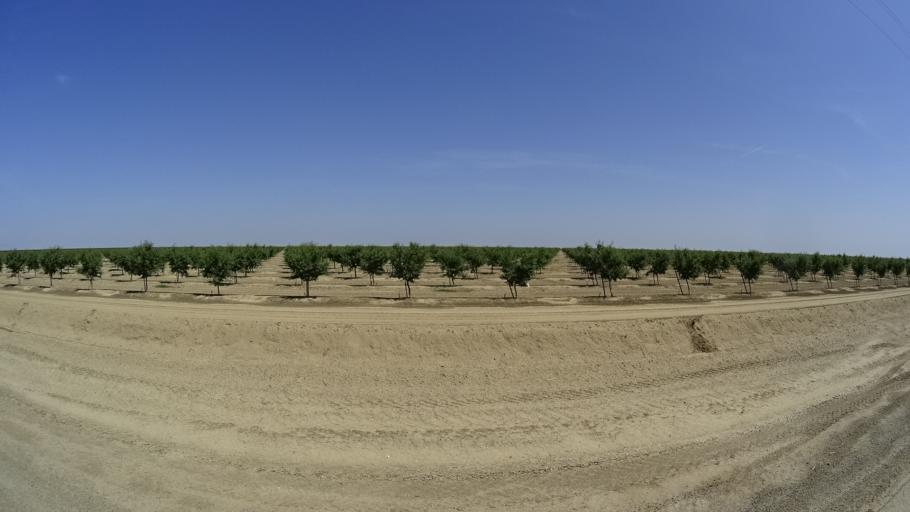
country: US
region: California
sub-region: Kings County
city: Kettleman City
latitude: 36.0943
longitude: -119.9787
